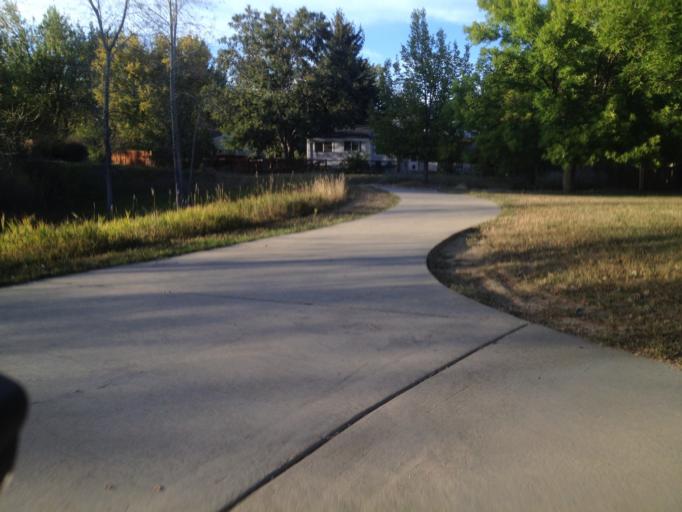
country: US
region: Colorado
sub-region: Boulder County
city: Louisville
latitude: 39.9838
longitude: -105.1421
